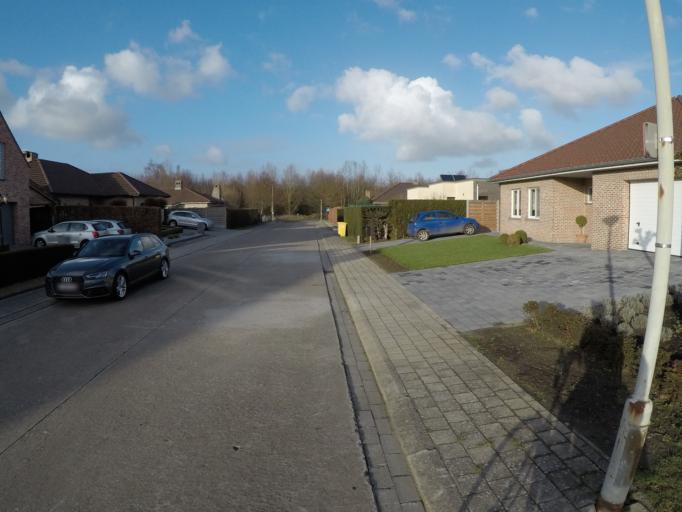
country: BE
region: Flanders
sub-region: Provincie Antwerpen
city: Lier
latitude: 51.1444
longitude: 4.6128
